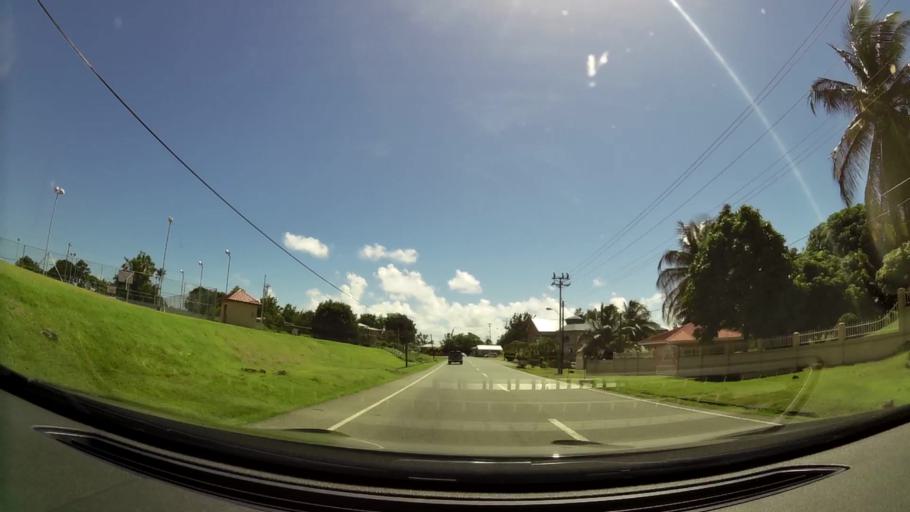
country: TT
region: Tobago
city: Scarborough
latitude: 11.1770
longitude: -60.7883
